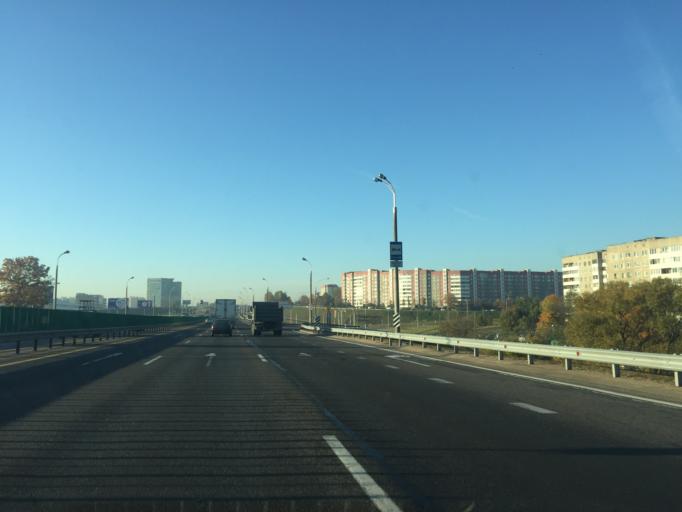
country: BY
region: Minsk
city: Vyaliki Trastsyanets
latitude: 53.8717
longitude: 27.6924
